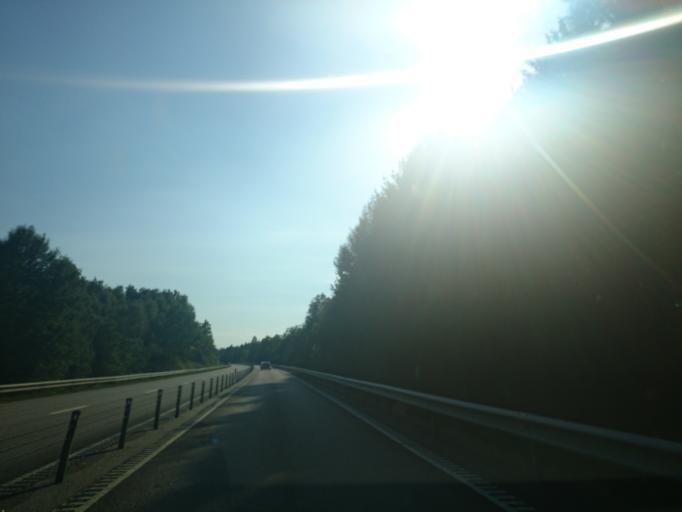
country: SE
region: Blekinge
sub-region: Karlshamns Kommun
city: Karlshamn
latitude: 56.2008
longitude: 14.9829
